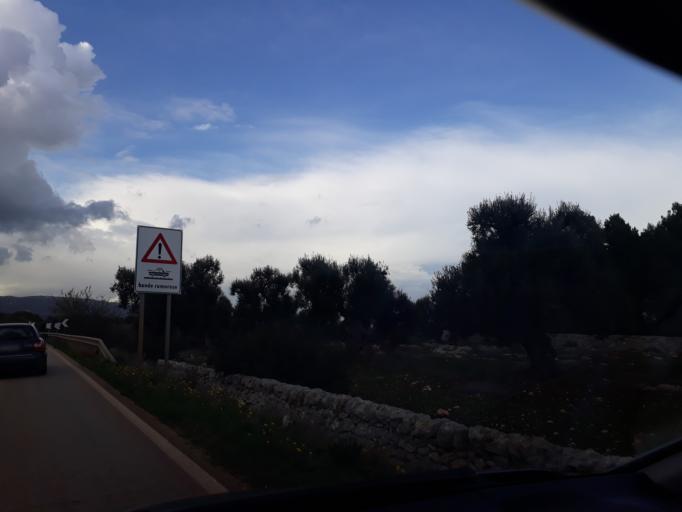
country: IT
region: Apulia
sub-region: Provincia di Brindisi
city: Pezze di Greco
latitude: 40.7994
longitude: 17.4068
